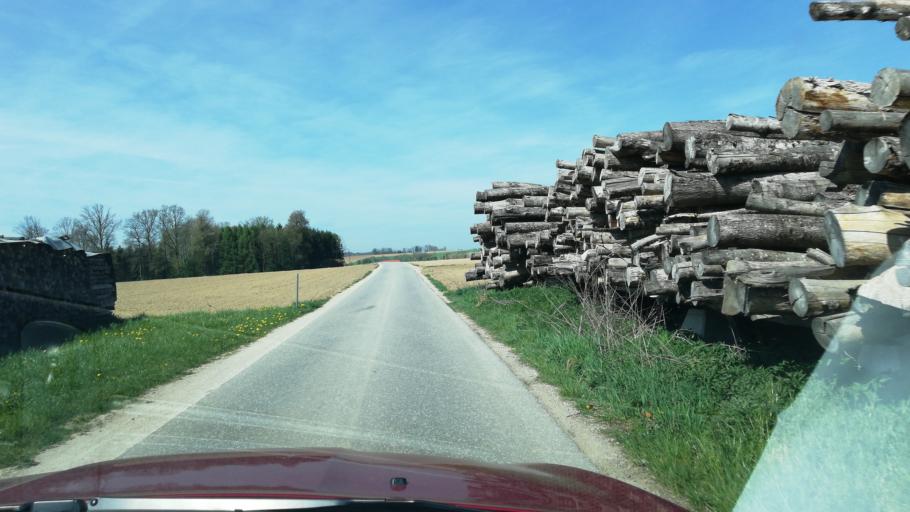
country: AT
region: Upper Austria
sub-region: Politischer Bezirk Steyr-Land
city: Pfarrkirchen bei Bad Hall
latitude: 48.0368
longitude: 14.1846
